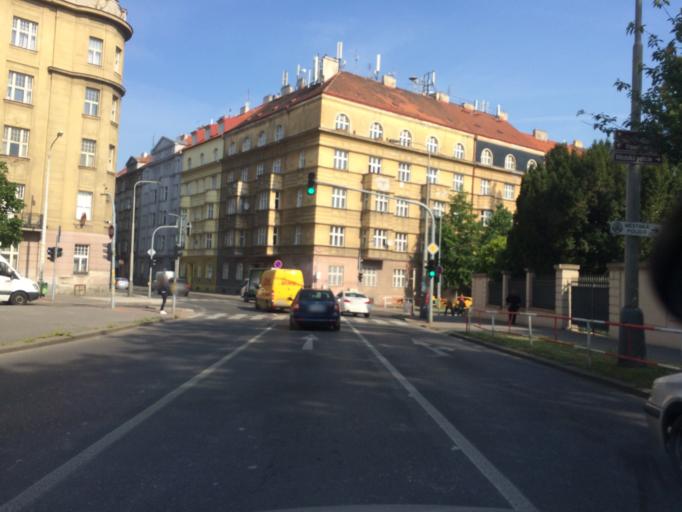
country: CZ
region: Praha
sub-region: Praha 1
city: Mala Strana
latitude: 50.0998
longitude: 14.4047
